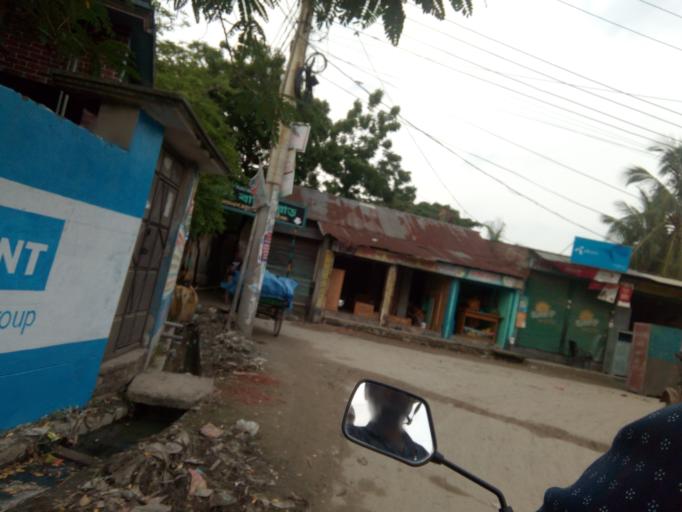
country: BD
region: Dhaka
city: Paltan
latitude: 23.7100
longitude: 90.4663
